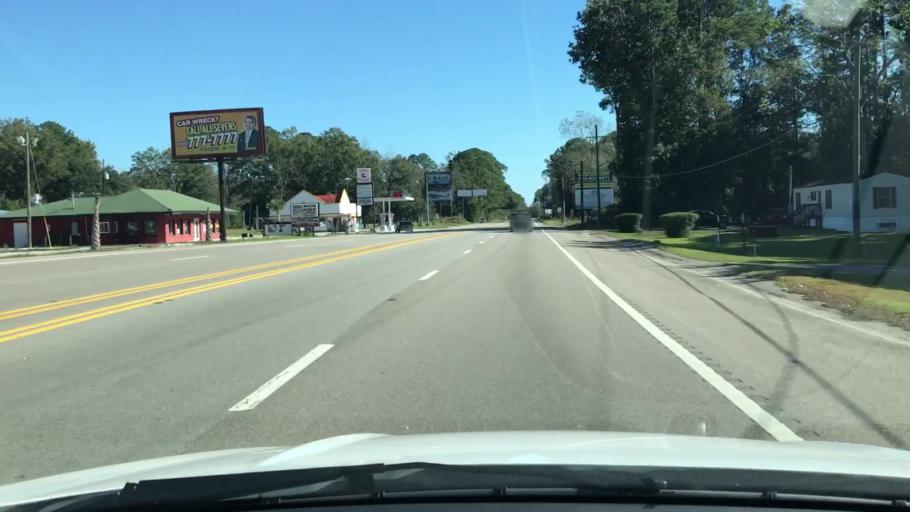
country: US
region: South Carolina
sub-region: Charleston County
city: Ravenel
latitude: 32.7733
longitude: -80.4592
